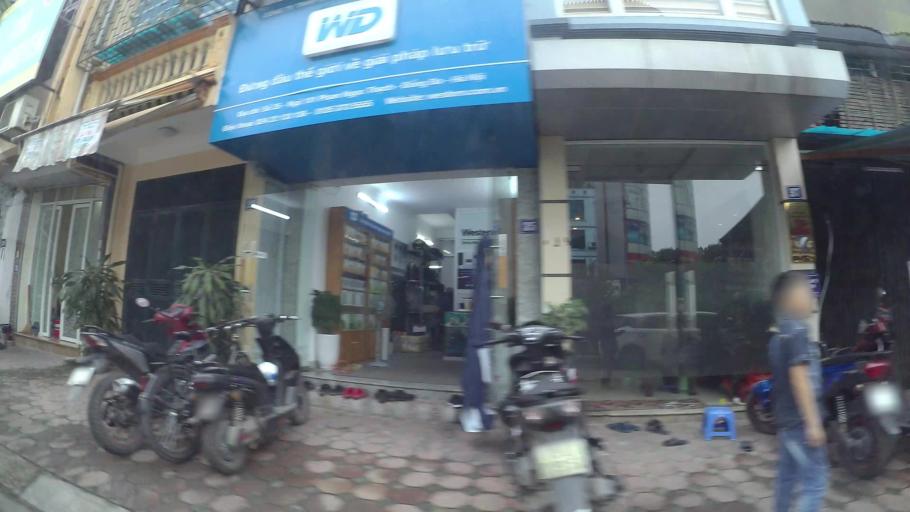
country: VN
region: Ha Noi
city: Dong Da
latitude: 21.0062
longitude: 105.8326
